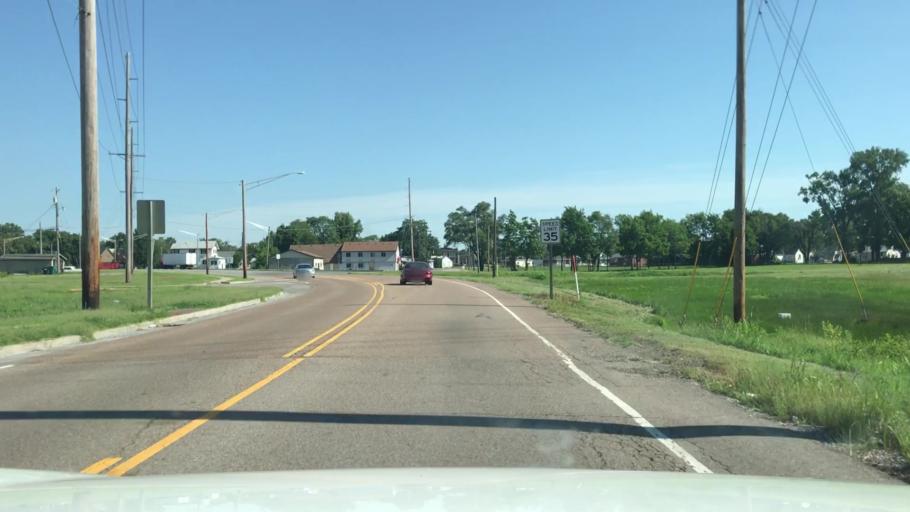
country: US
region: Illinois
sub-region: Madison County
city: Venice
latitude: 38.6681
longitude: -90.1702
